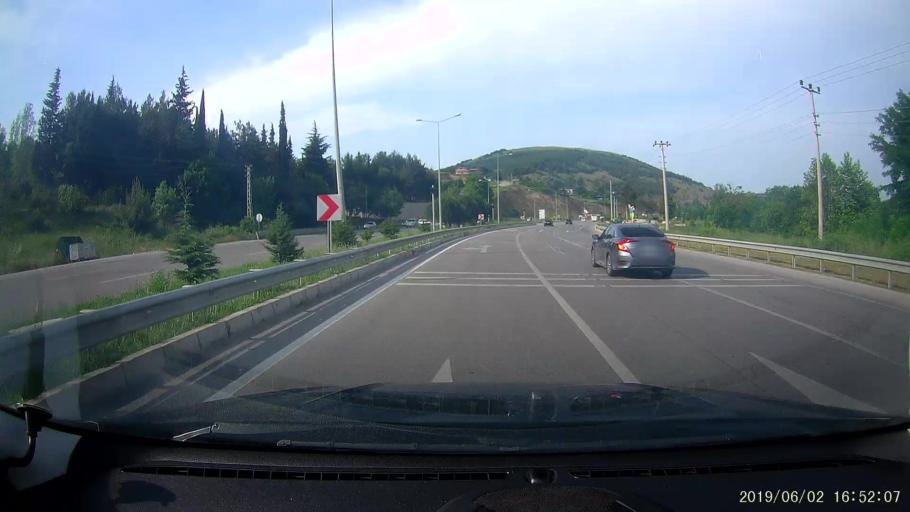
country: TR
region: Samsun
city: Samsun
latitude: 41.2834
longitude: 36.1923
